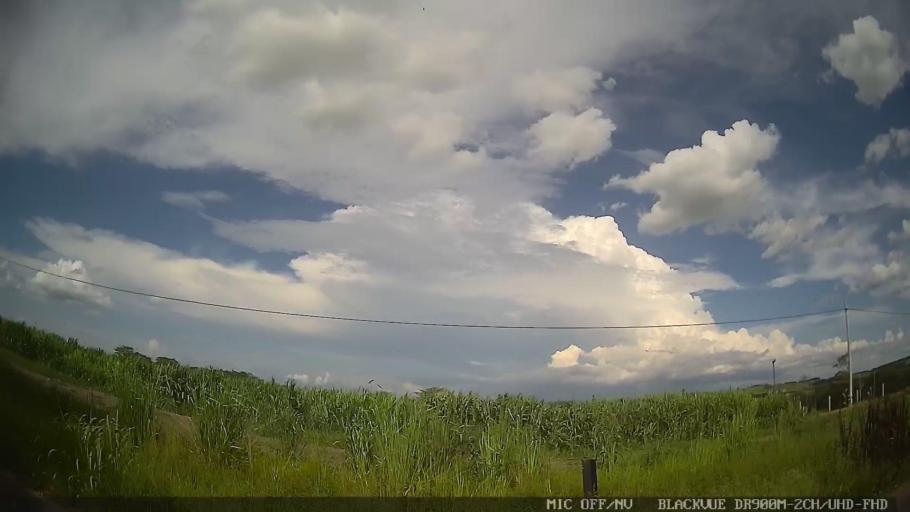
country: BR
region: Sao Paulo
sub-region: Conchas
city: Conchas
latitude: -23.0488
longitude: -47.9586
